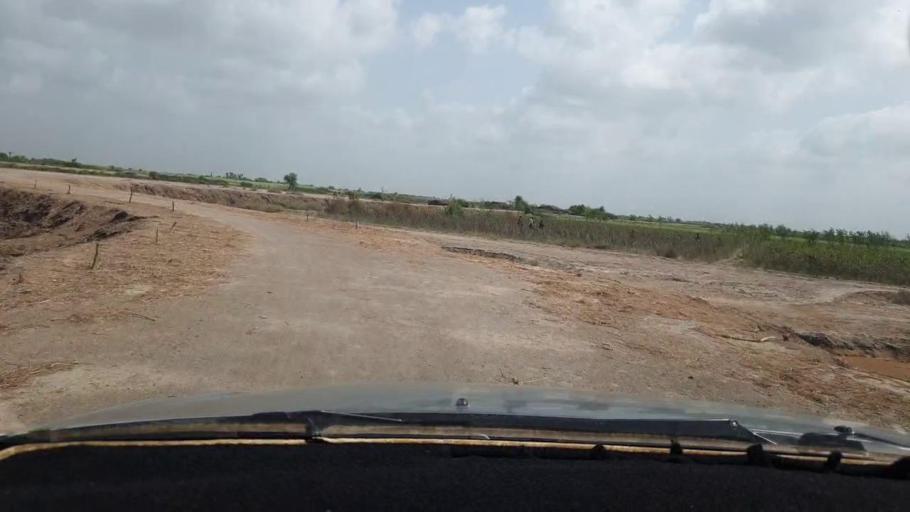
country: PK
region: Sindh
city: Tando Bago
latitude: 24.7202
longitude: 69.1436
